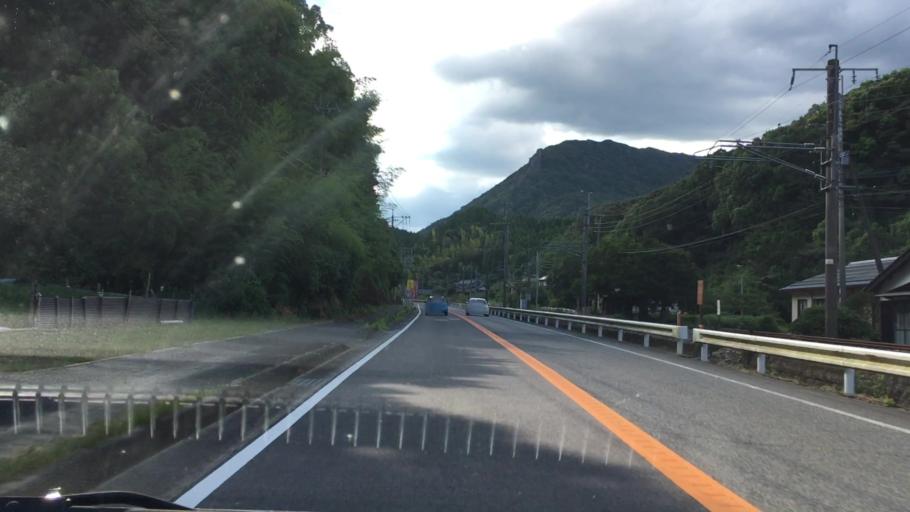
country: JP
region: Saga Prefecture
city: Imaricho-ko
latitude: 33.1911
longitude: 129.9208
